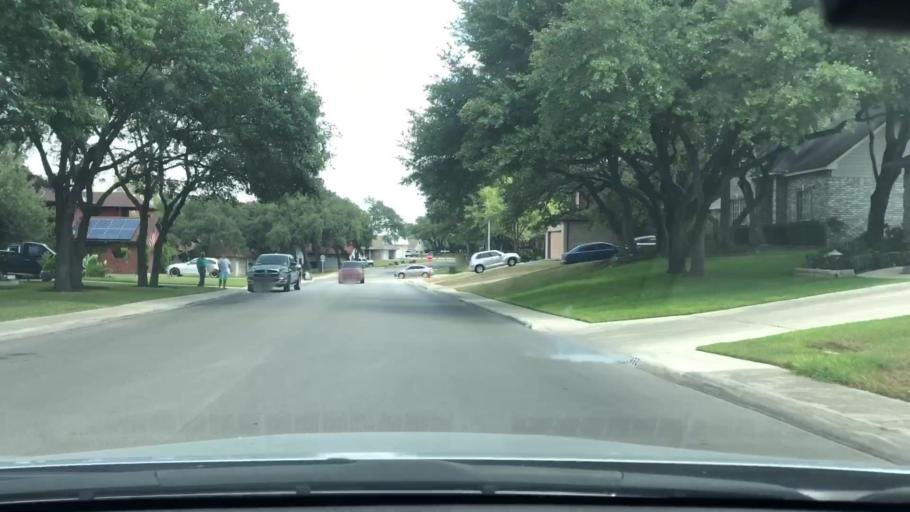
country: US
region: Texas
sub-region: Bexar County
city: Live Oak
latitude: 29.5708
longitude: -98.3207
